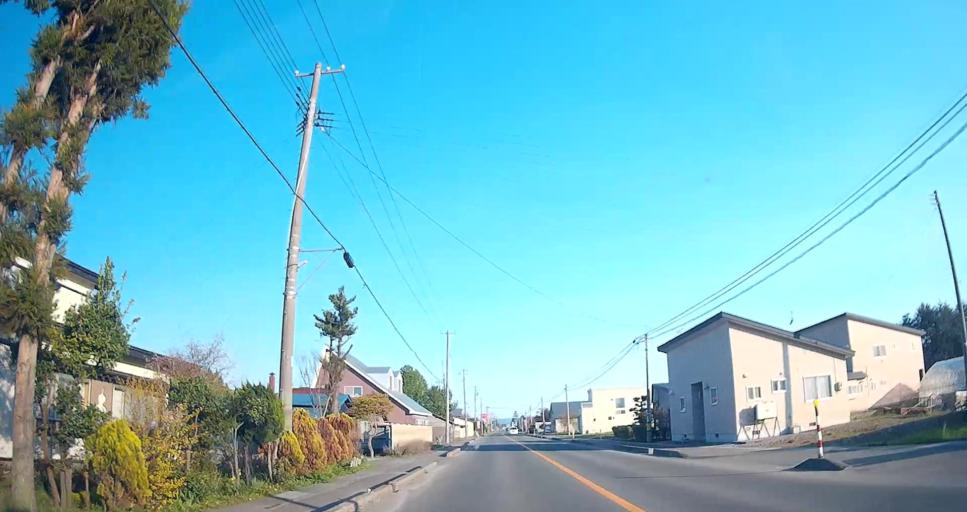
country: JP
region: Aomori
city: Mutsu
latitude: 41.2683
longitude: 141.2202
